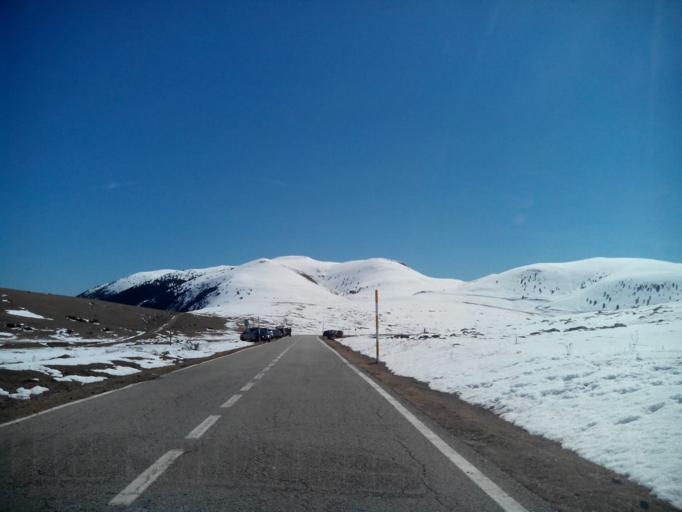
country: ES
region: Catalonia
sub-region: Provincia de Girona
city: Toses
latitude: 42.3204
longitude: 1.9664
